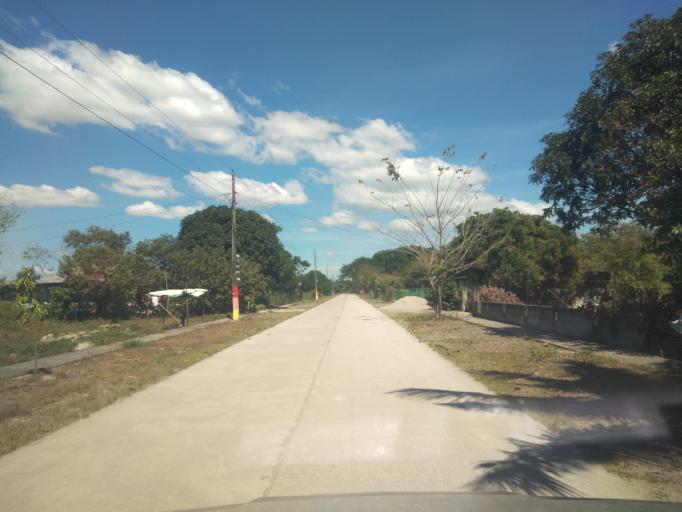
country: PH
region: Central Luzon
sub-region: Province of Pampanga
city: San Basilio
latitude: 15.0304
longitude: 120.6058
